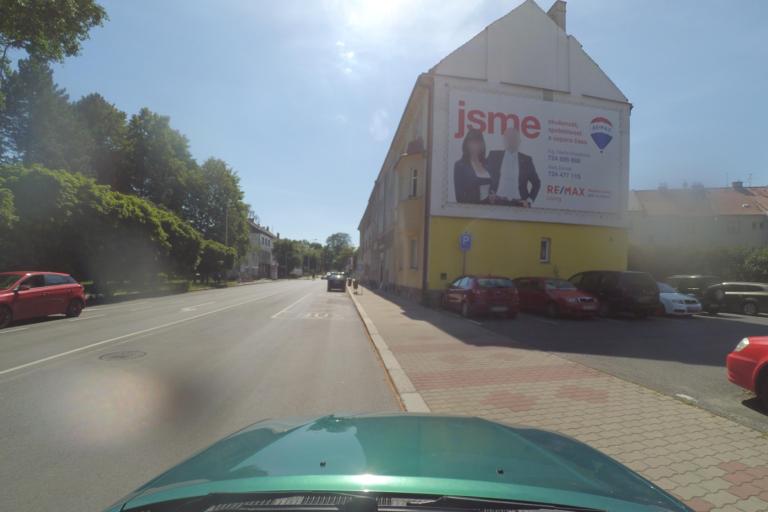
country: CZ
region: Liberecky
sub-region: Okres Ceska Lipa
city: Ceska Lipa
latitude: 50.6793
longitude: 14.5359
